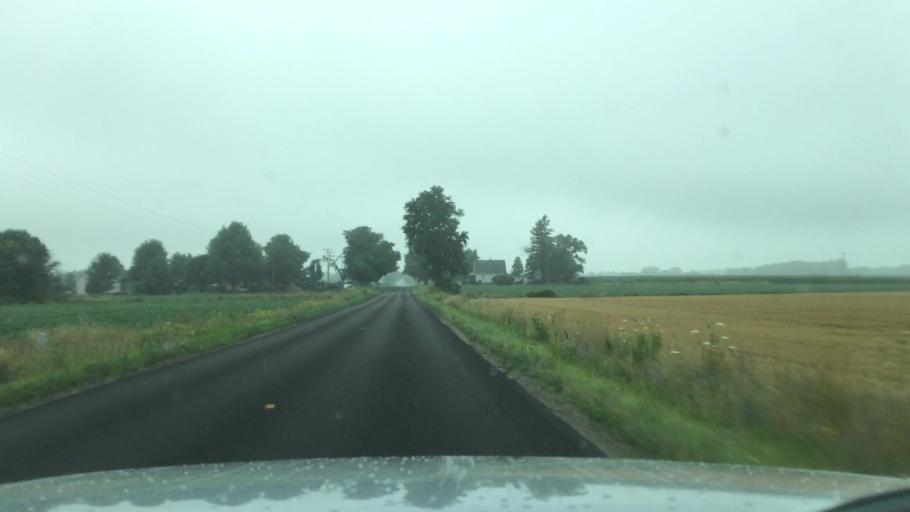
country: US
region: Michigan
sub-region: Shiawassee County
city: New Haven
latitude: 43.0574
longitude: -84.1353
